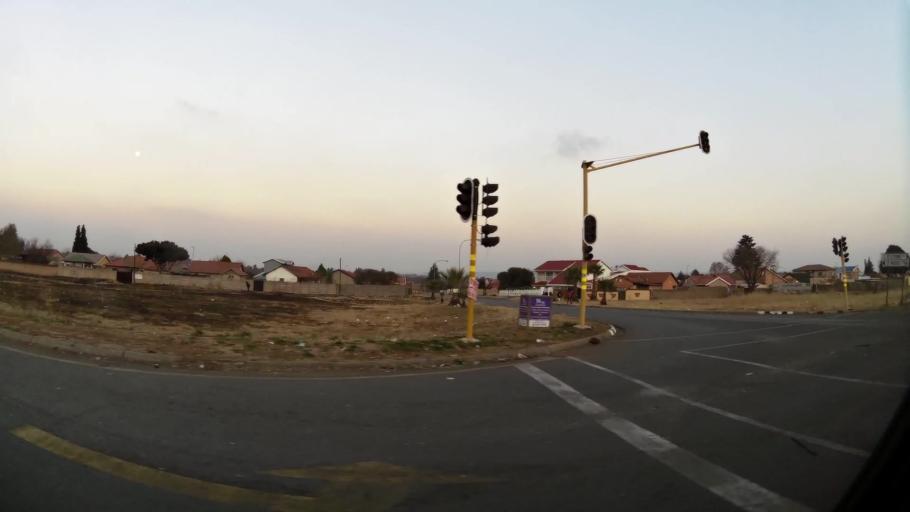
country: ZA
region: Gauteng
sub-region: City of Johannesburg Metropolitan Municipality
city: Soweto
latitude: -26.2940
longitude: 27.8760
